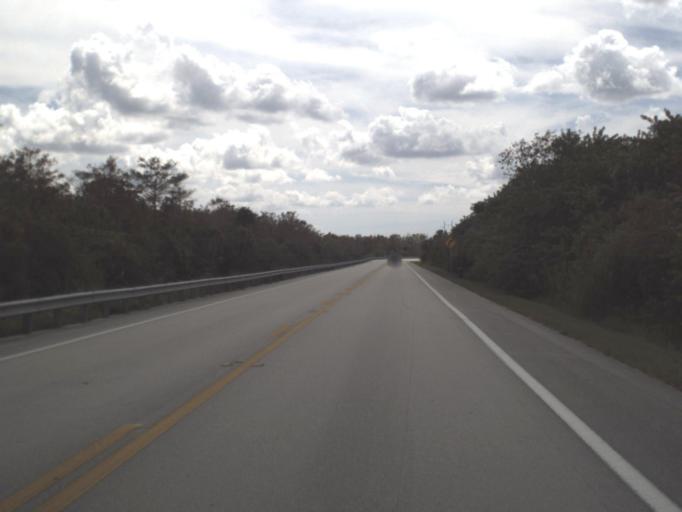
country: US
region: Florida
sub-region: Collier County
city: Marco
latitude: 25.9244
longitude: -81.3580
